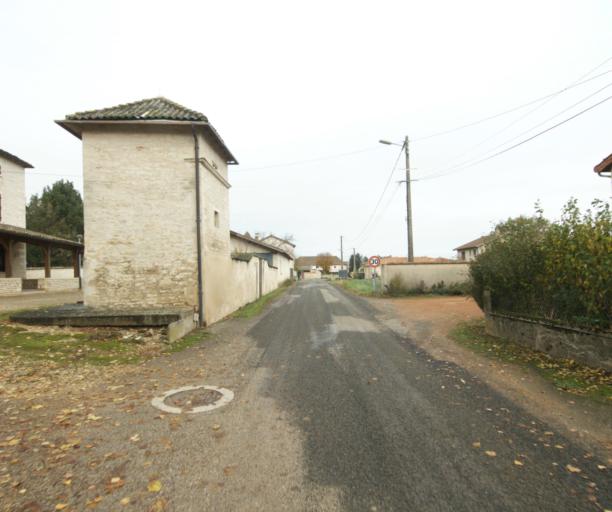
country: FR
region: Rhone-Alpes
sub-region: Departement de l'Ain
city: Pont-de-Vaux
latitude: 46.4635
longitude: 4.8823
